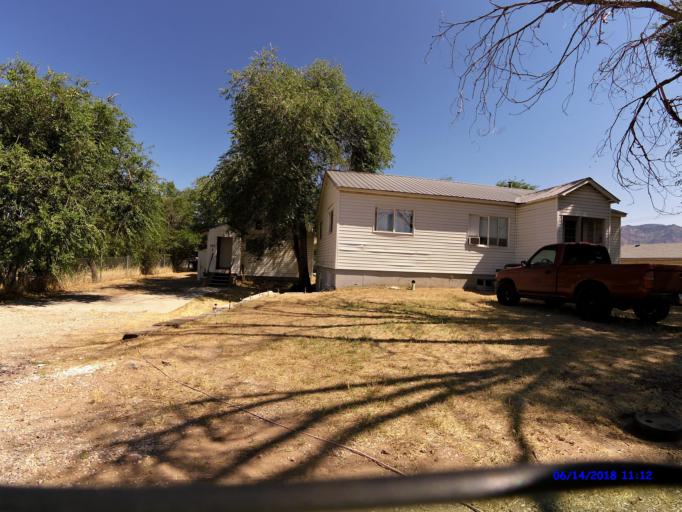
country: US
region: Utah
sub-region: Weber County
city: Ogden
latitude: 41.2186
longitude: -111.9979
